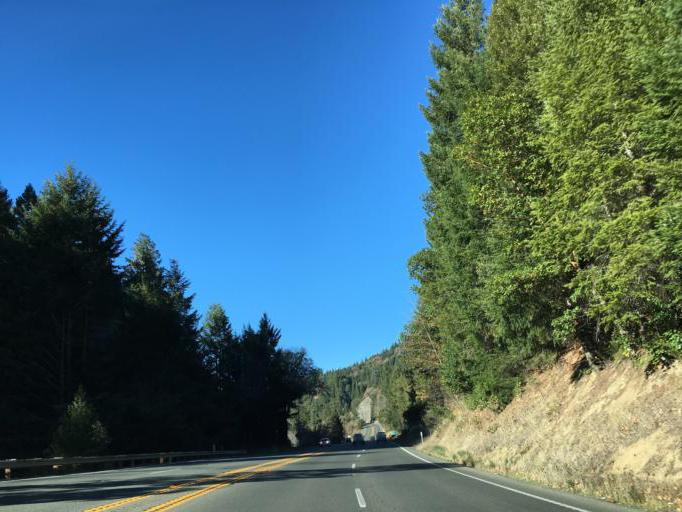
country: US
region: California
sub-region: Mendocino County
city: Brooktrails
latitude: 39.5155
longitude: -123.3902
